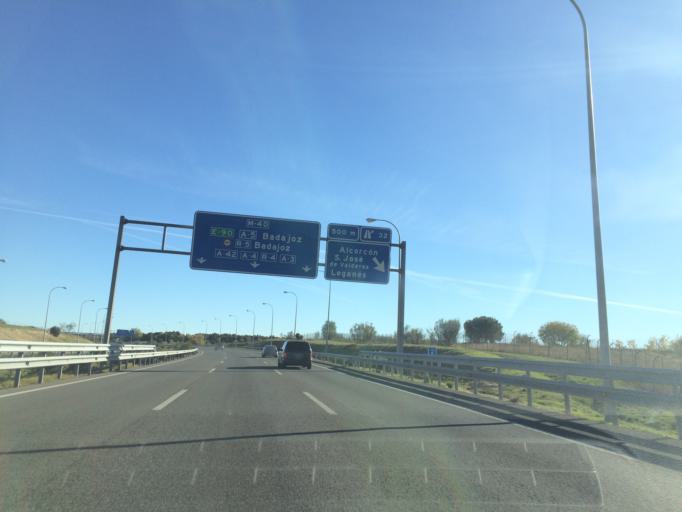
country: ES
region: Madrid
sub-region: Provincia de Madrid
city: Alcorcon
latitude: 40.3784
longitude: -3.8090
